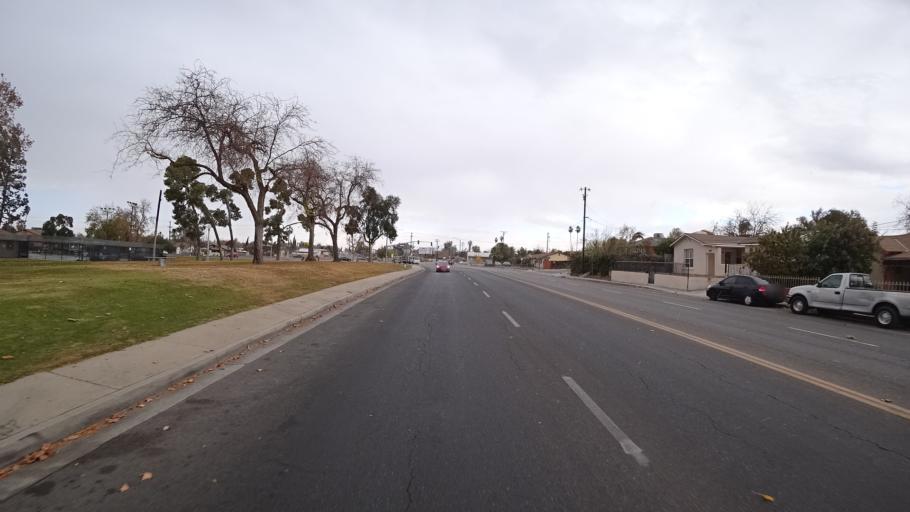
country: US
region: California
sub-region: Kern County
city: Bakersfield
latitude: 35.3892
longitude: -118.9852
